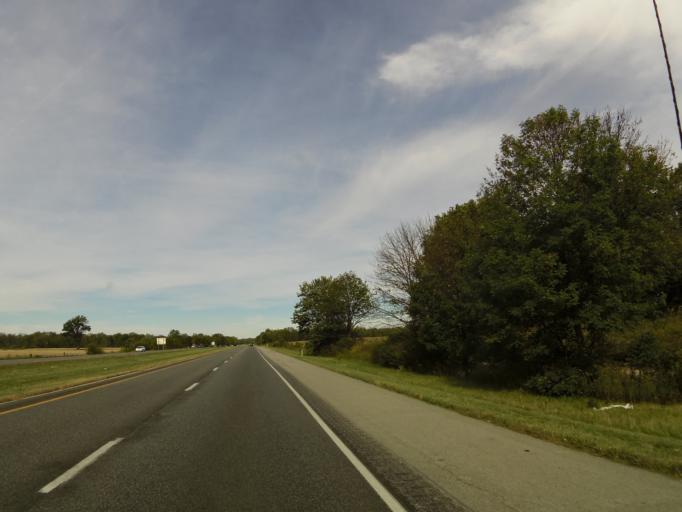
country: US
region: Indiana
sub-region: Hendricks County
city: Brownsburg
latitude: 39.8665
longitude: -86.4154
